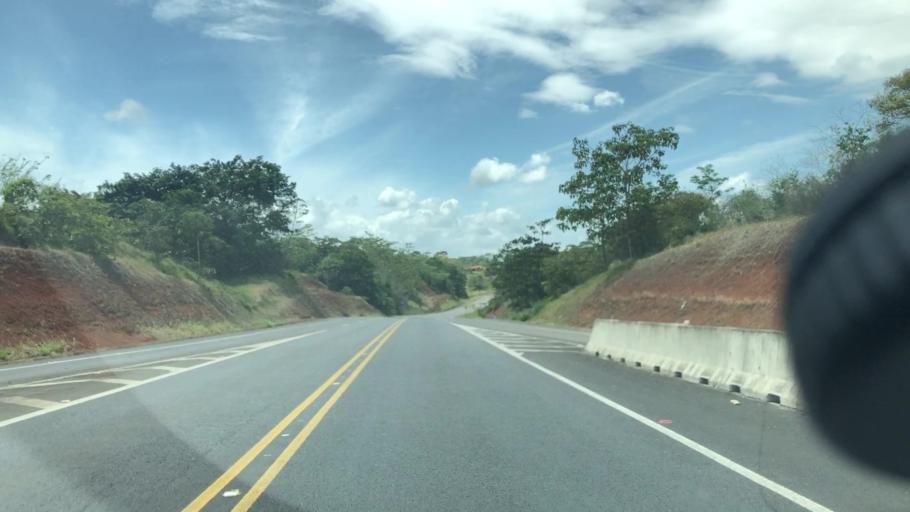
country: CR
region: Heredia
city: La Virgen
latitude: 10.4401
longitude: -84.1611
